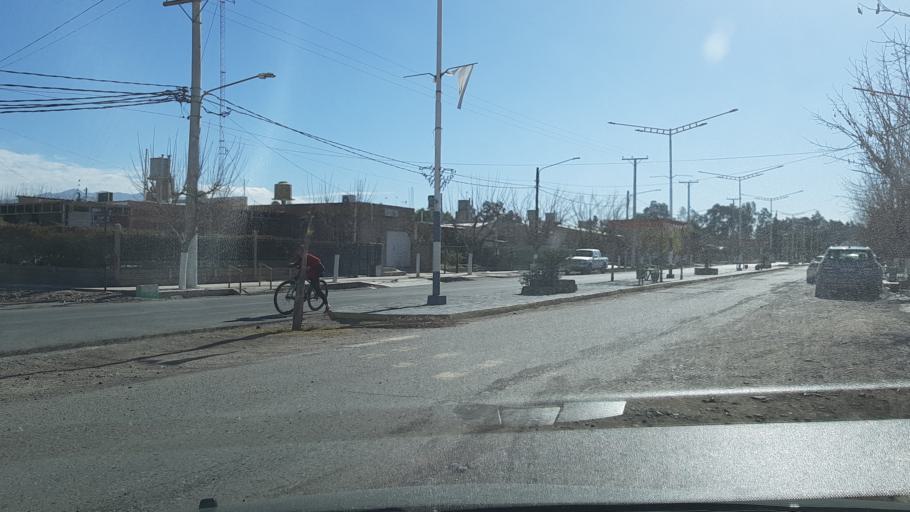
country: AR
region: San Juan
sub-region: Departamento de Zonda
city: Zonda
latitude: -31.5480
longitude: -68.7318
